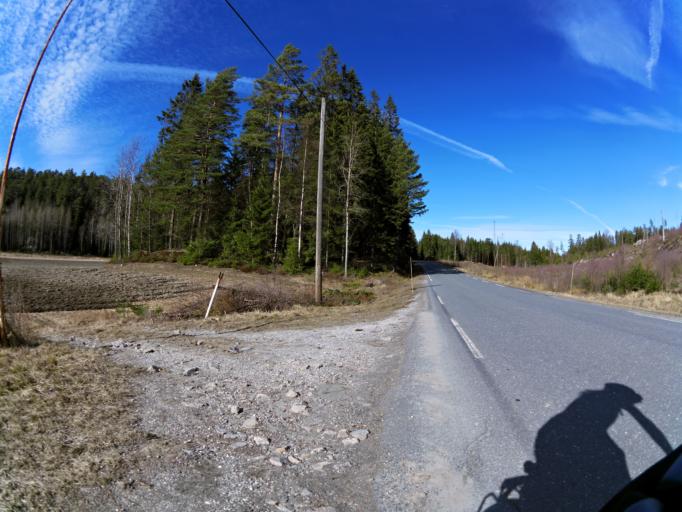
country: NO
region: Ostfold
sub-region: Fredrikstad
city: Fredrikstad
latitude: 59.2707
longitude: 10.9401
